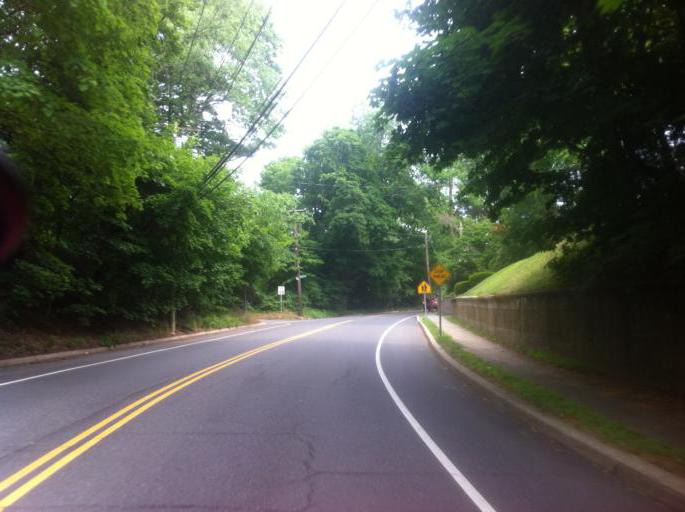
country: US
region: New York
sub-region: Nassau County
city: Locust Valley
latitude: 40.8785
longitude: -73.5799
